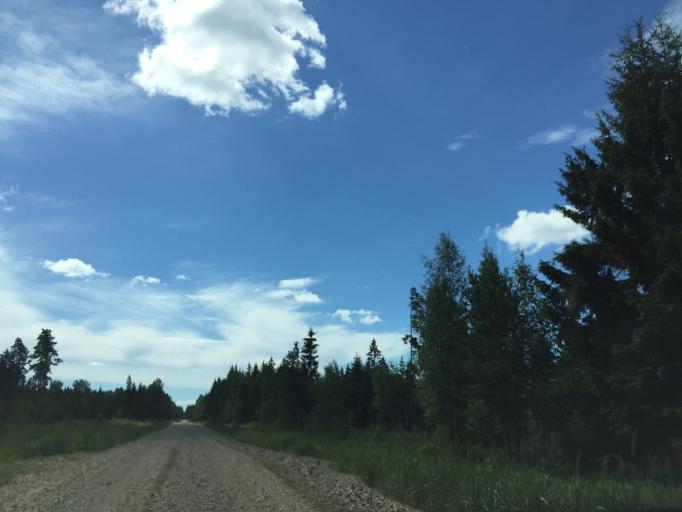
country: LV
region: Ventspils Rajons
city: Piltene
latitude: 57.2600
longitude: 21.8375
